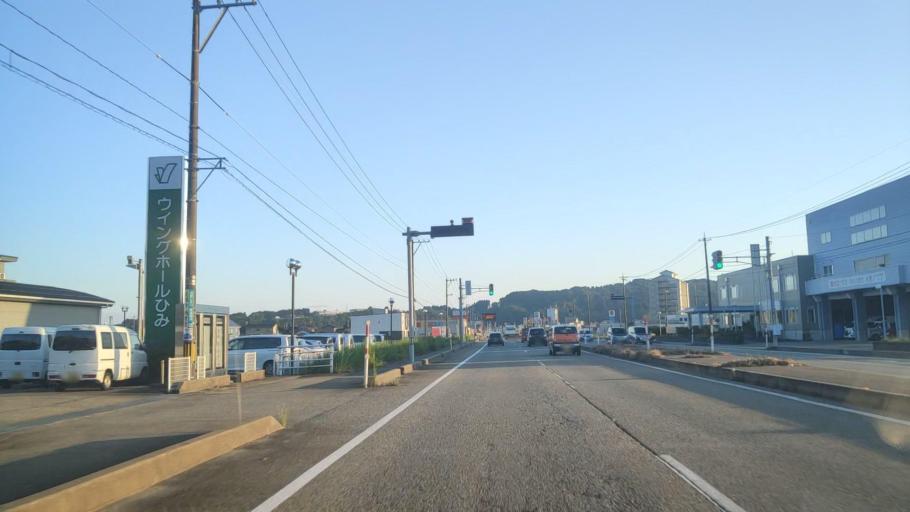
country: JP
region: Toyama
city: Himi
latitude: 36.8670
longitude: 136.9755
